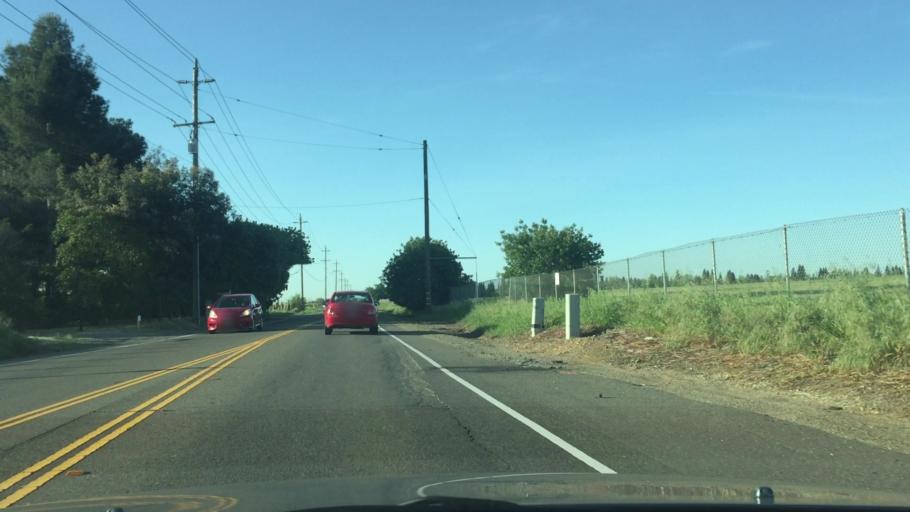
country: US
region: California
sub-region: Sacramento County
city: Elk Grove
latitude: 38.4216
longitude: -121.3532
